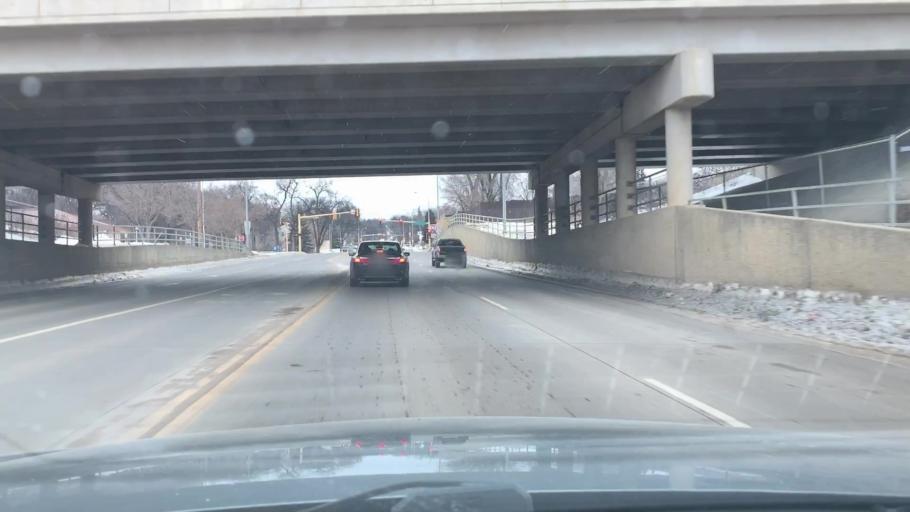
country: US
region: North Dakota
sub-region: Burleigh County
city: Bismarck
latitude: 46.8054
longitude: -100.7944
